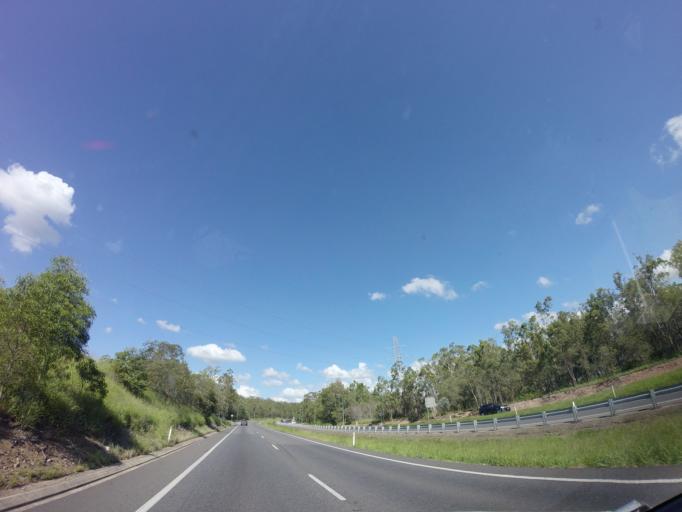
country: AU
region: Queensland
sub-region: Ipswich
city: Tivoli
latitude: -27.5741
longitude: 152.7912
